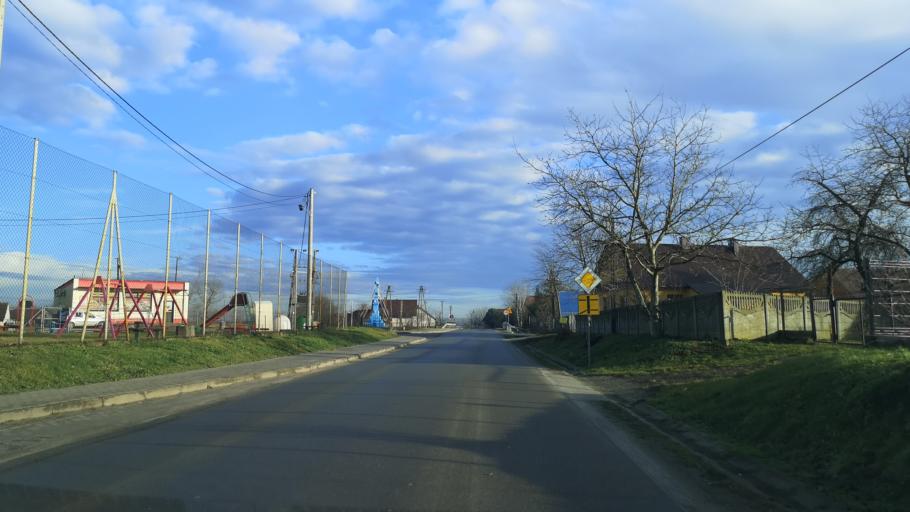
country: PL
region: Subcarpathian Voivodeship
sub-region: Powiat lezajski
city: Wierzawice
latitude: 50.2478
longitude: 22.4661
